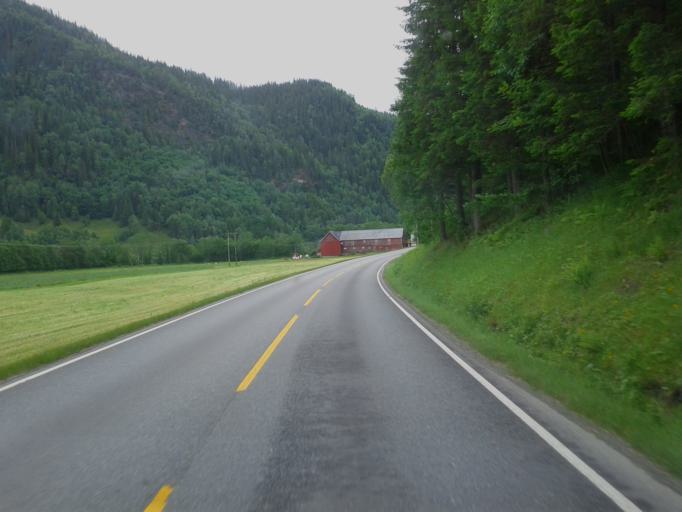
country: NO
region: Sor-Trondelag
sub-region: Midtre Gauldal
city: Storen
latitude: 62.9677
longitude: 10.5742
